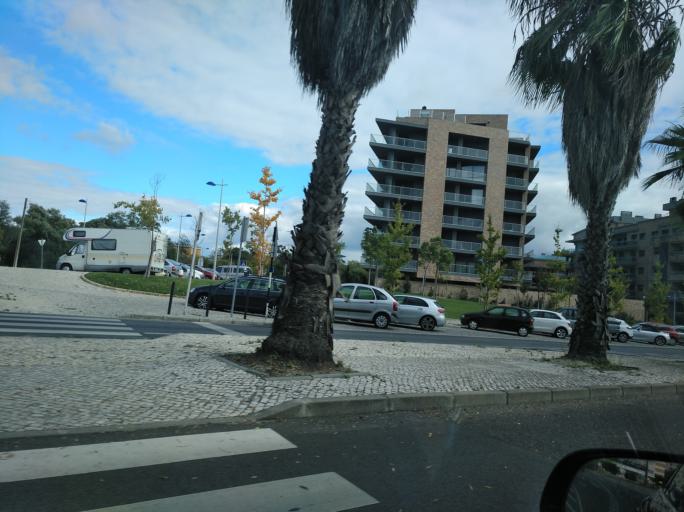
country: PT
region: Lisbon
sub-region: Loures
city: Moscavide
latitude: 38.7784
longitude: -9.1108
